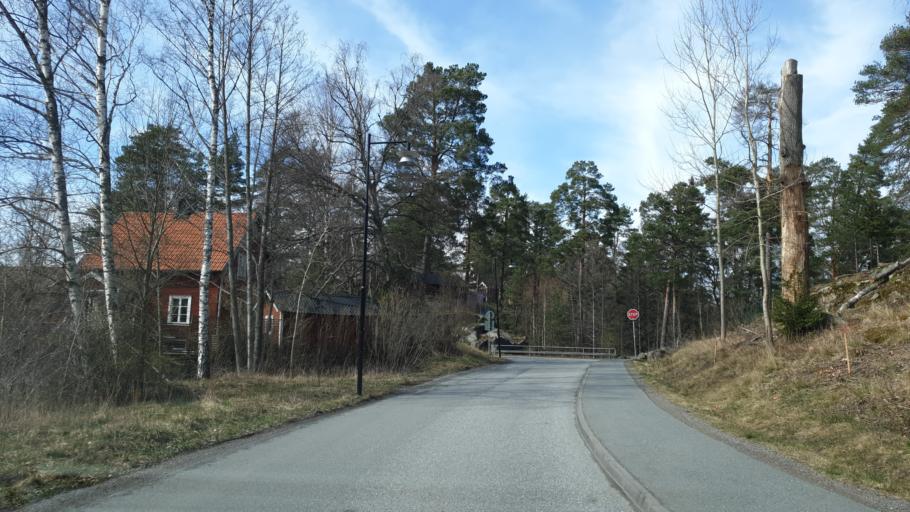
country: SE
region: Stockholm
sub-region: Nacka Kommun
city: Boo
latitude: 59.3342
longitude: 18.2924
